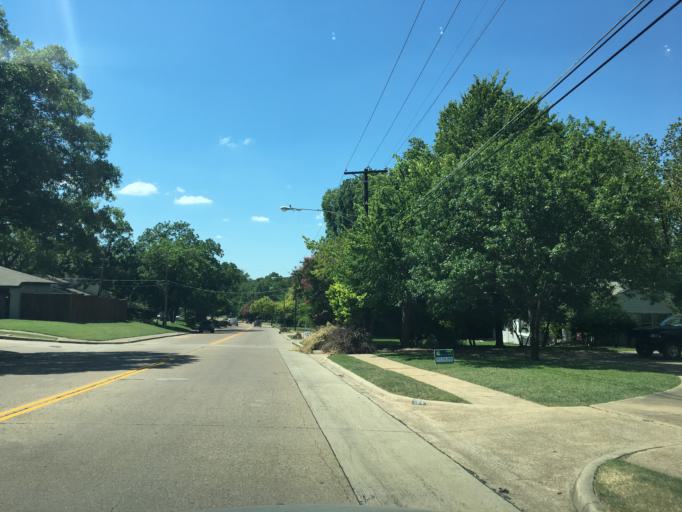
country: US
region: Texas
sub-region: Dallas County
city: Highland Park
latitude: 32.8421
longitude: -96.7002
